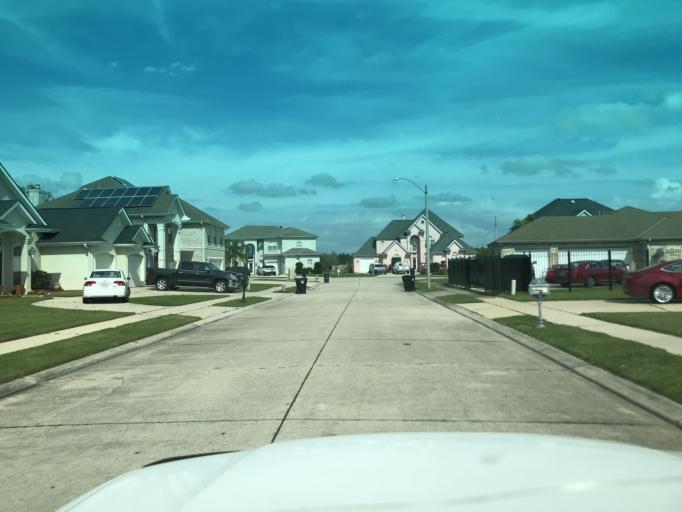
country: US
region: Louisiana
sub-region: Saint Bernard Parish
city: Chalmette
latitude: 30.0374
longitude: -89.9517
